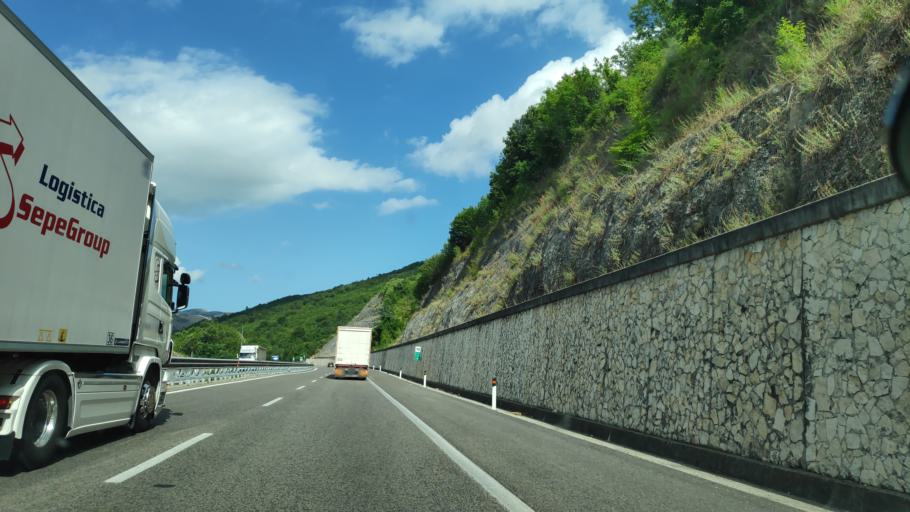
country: IT
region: Campania
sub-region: Provincia di Salerno
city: Pertosa
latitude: 40.5312
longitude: 15.4483
